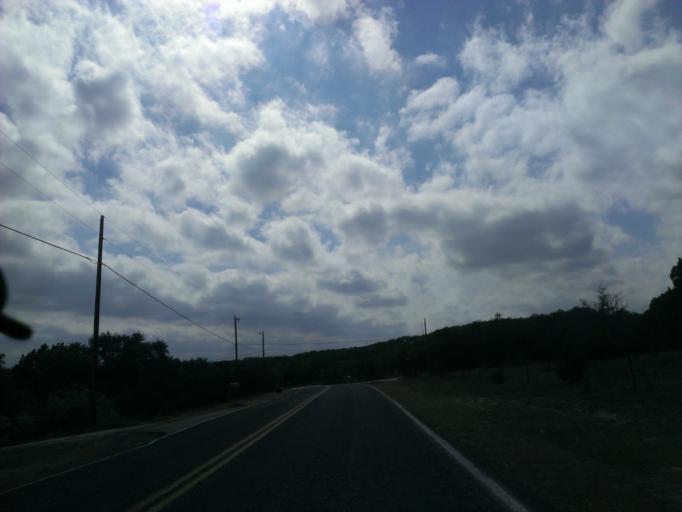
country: US
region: Texas
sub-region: Travis County
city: Briarcliff
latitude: 30.3792
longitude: -98.0940
